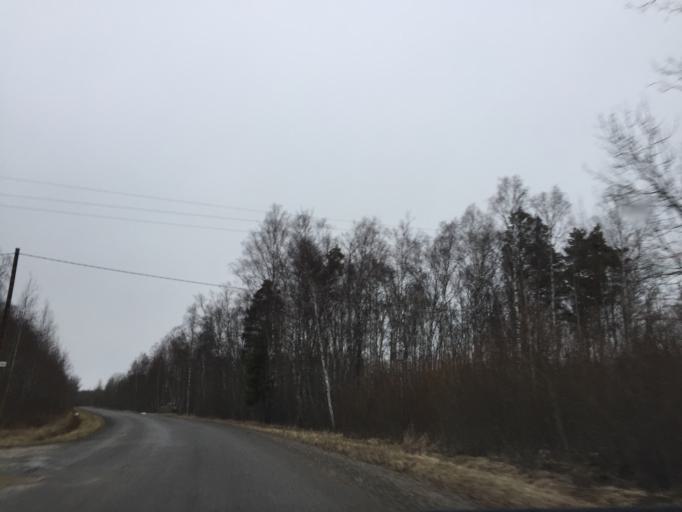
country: EE
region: Laeaene
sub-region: Lihula vald
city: Lihula
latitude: 58.6282
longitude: 23.6333
